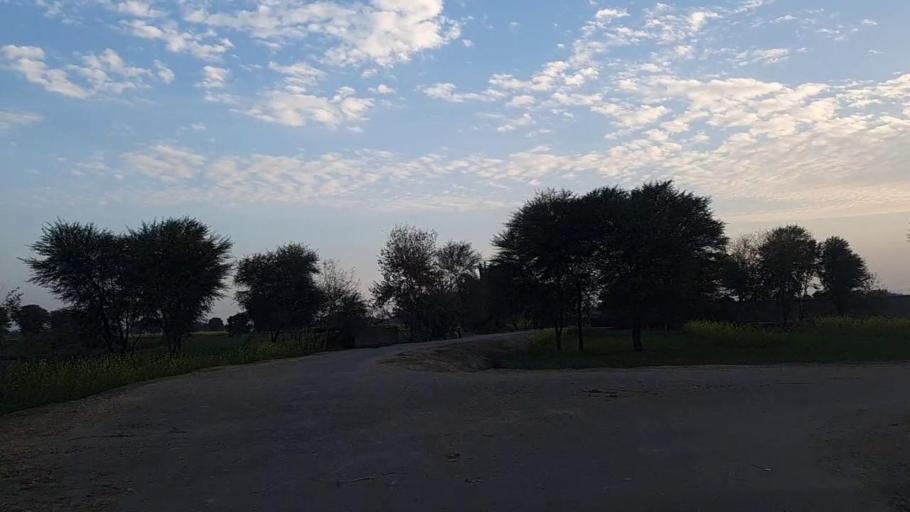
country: PK
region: Sindh
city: Daur
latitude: 26.4145
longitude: 68.4779
